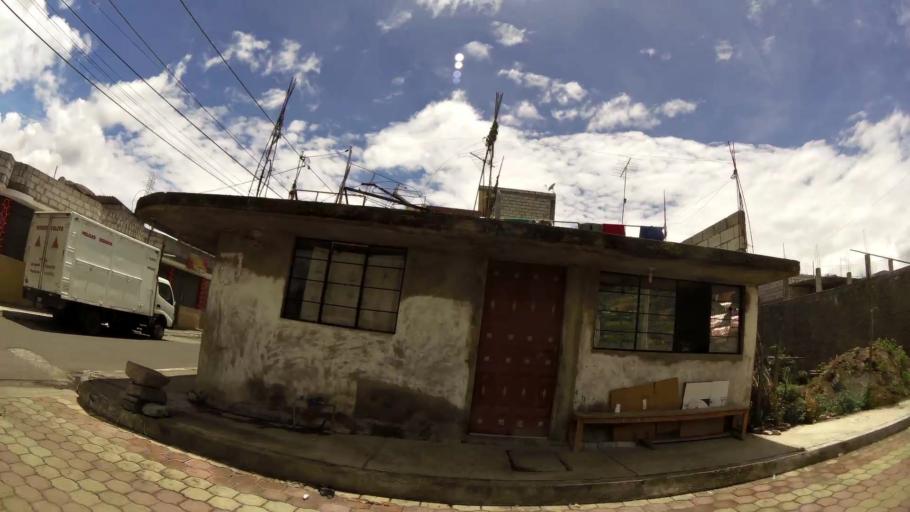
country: EC
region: Tungurahua
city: Pelileo
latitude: -1.3286
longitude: -78.5280
